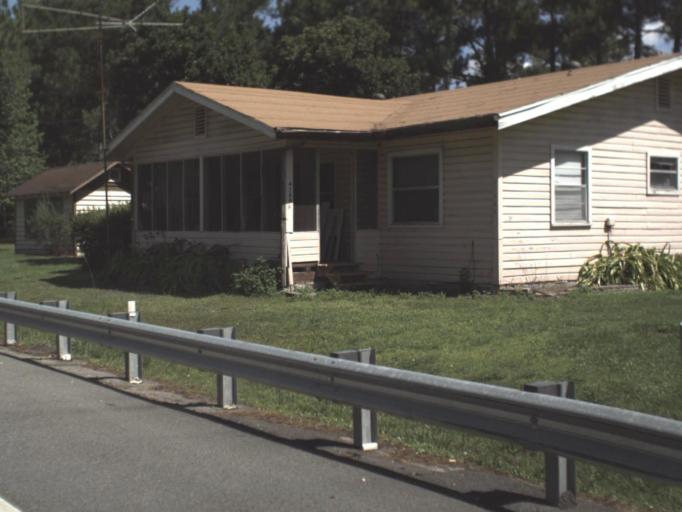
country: US
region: Florida
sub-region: Putnam County
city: Palatka
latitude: 29.6748
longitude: -81.7130
